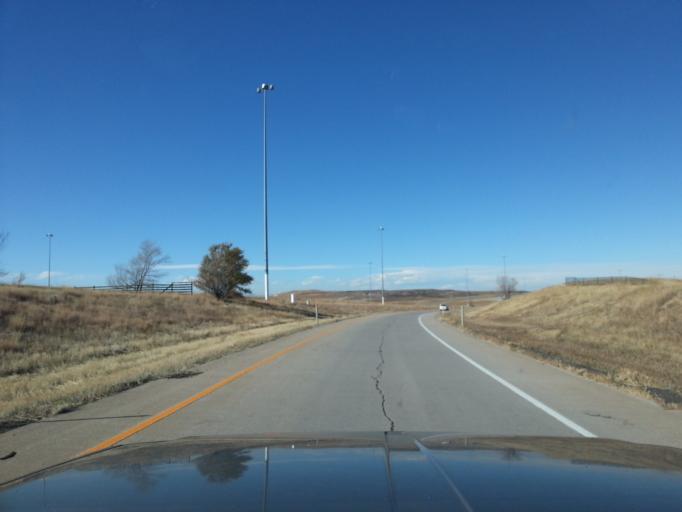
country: US
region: Colorado
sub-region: Adams County
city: Aurora
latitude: 39.8367
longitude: -104.7446
